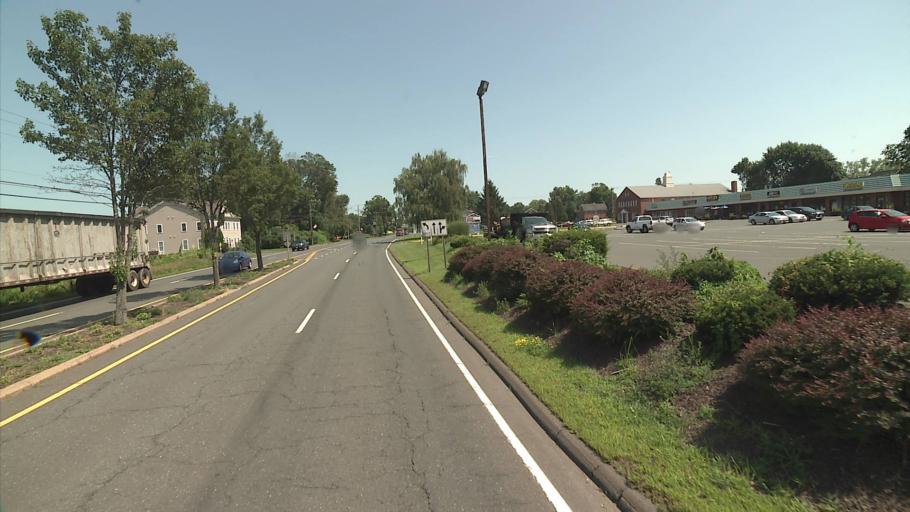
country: US
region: Connecticut
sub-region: Hartford County
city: Tariffville
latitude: 41.9435
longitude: -72.7283
